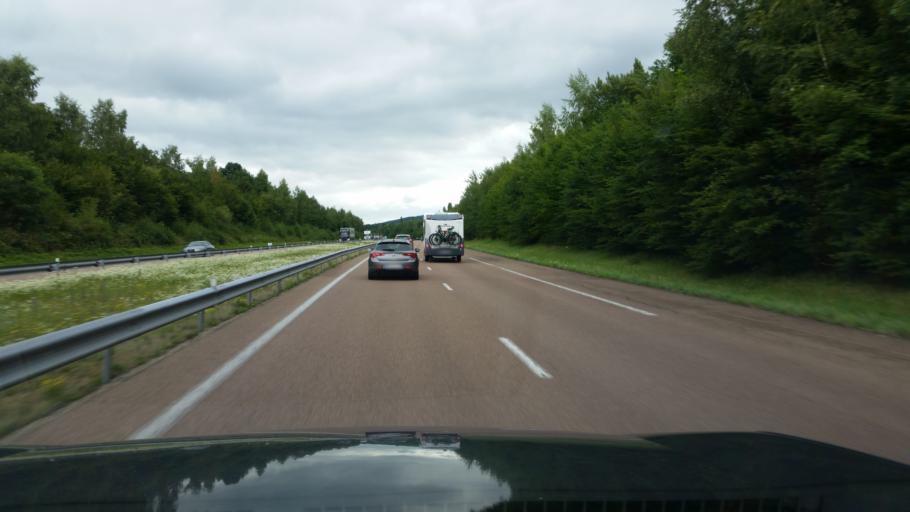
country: FR
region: Franche-Comte
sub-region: Departement du Jura
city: Bletterans
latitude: 46.7130
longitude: 5.4887
